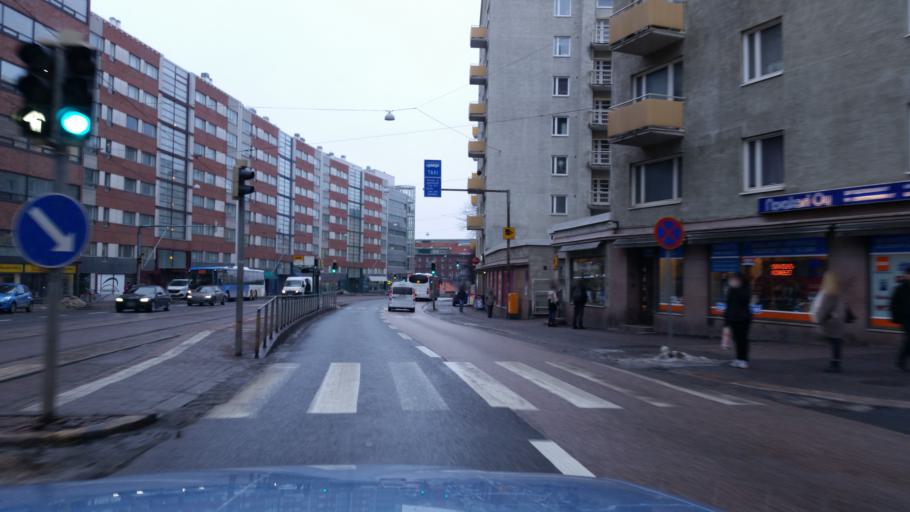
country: FI
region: Uusimaa
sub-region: Helsinki
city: Helsinki
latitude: 60.1860
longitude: 24.9612
